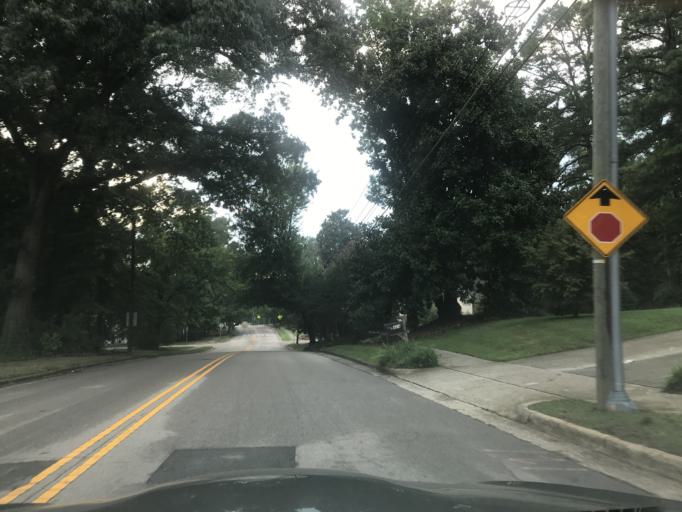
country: US
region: North Carolina
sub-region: Wake County
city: West Raleigh
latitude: 35.8443
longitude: -78.6478
